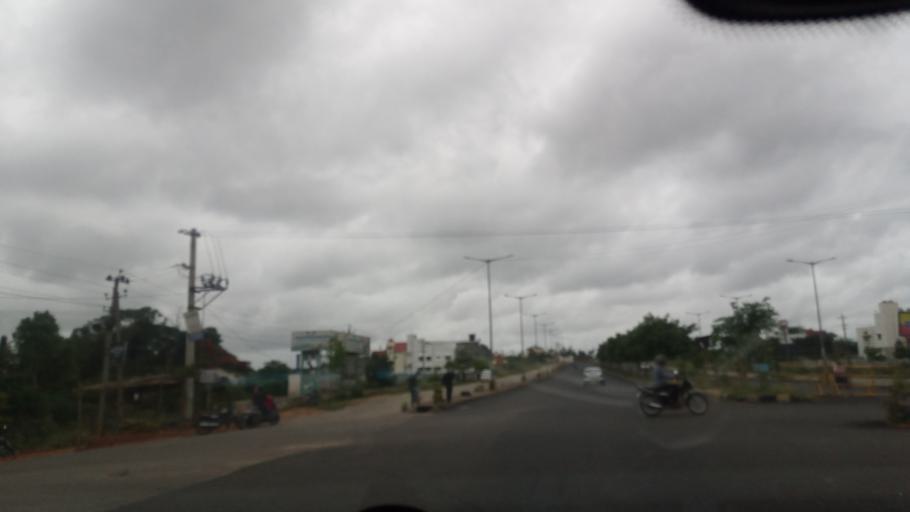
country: IN
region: Karnataka
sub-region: Mysore
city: Mysore
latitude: 12.3215
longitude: 76.5961
